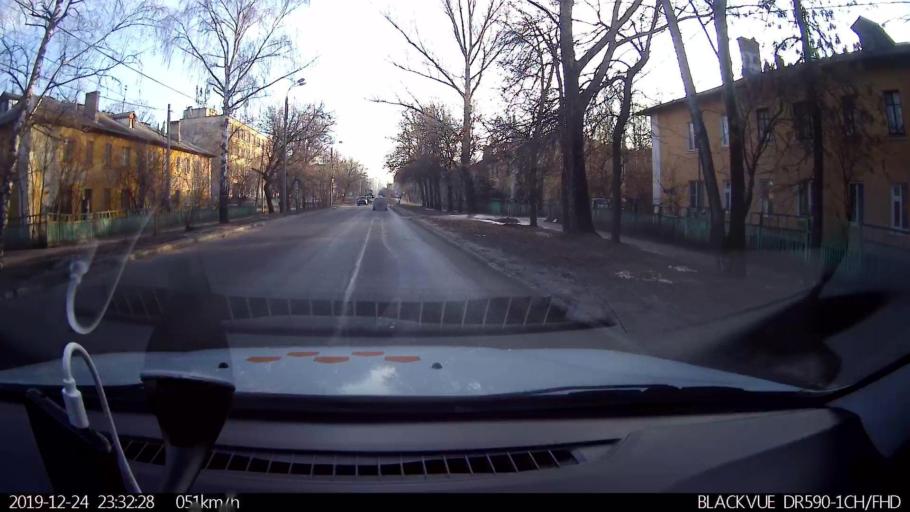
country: RU
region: Nizjnij Novgorod
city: Burevestnik
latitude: 56.2284
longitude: 43.8509
